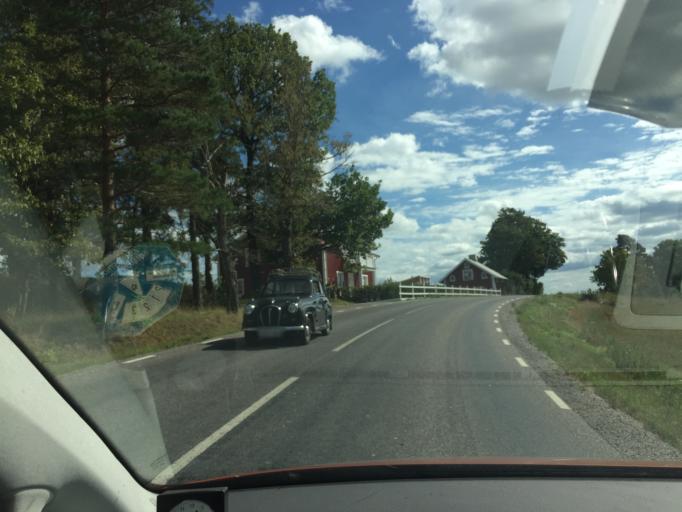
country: SE
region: OErebro
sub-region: Hallsbergs Kommun
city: Hallsberg
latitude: 59.1162
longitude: 15.0093
